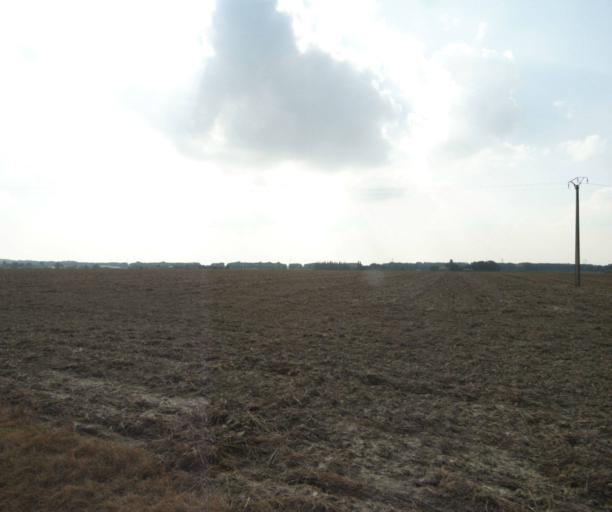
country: FR
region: Nord-Pas-de-Calais
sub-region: Departement du Nord
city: Houplin-Ancoisne
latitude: 50.5711
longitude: 2.9960
